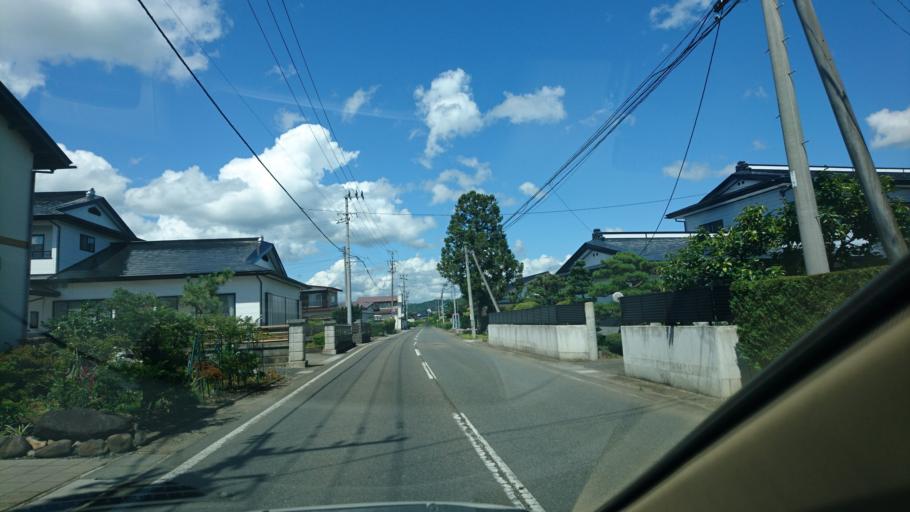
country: JP
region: Iwate
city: Kitakami
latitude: 39.3262
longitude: 141.1407
